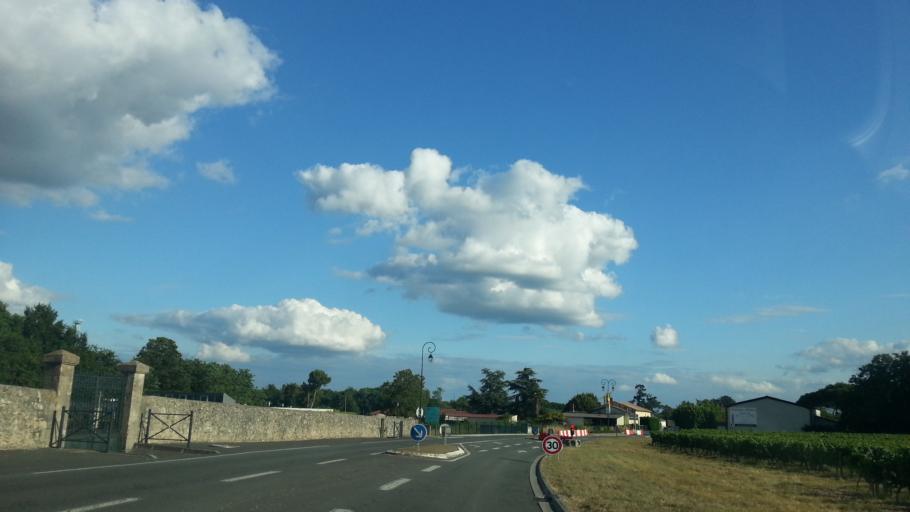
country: FR
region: Aquitaine
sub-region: Departement de la Gironde
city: Illats
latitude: 44.6028
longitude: -0.3705
